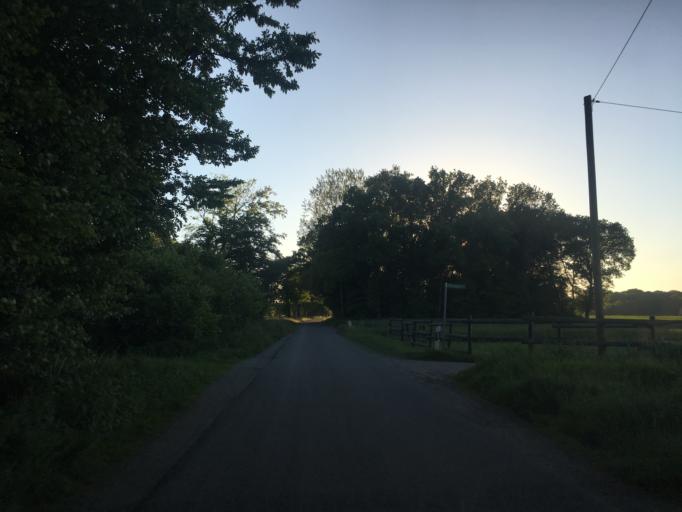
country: DE
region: North Rhine-Westphalia
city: Ludinghausen
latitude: 51.7422
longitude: 7.4465
